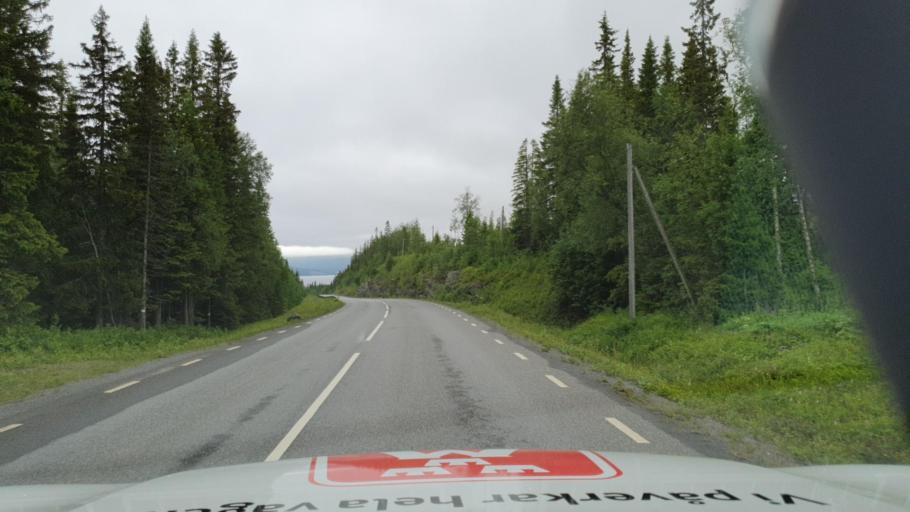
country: SE
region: Jaemtland
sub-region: Are Kommun
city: Are
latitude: 63.5321
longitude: 13.0725
